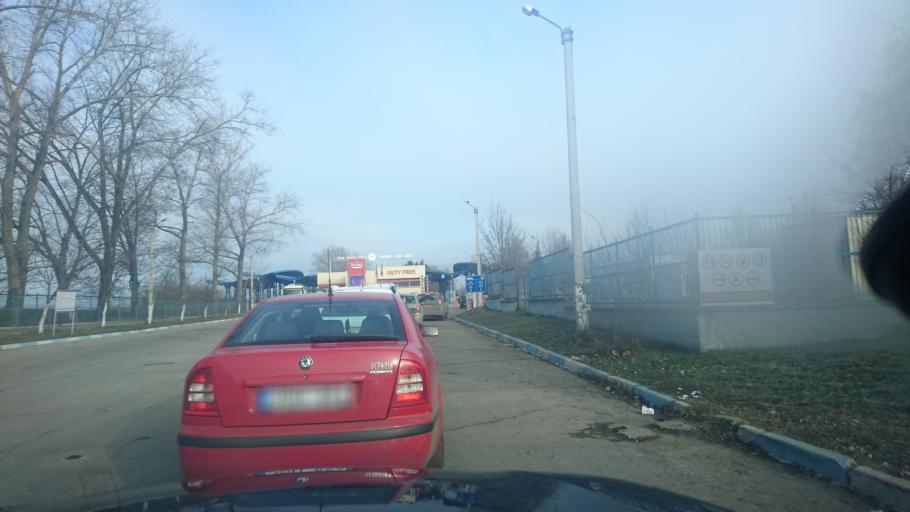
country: RO
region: Botosani
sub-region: Comuna Paltinis
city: Paltinis
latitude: 48.2651
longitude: 26.6255
